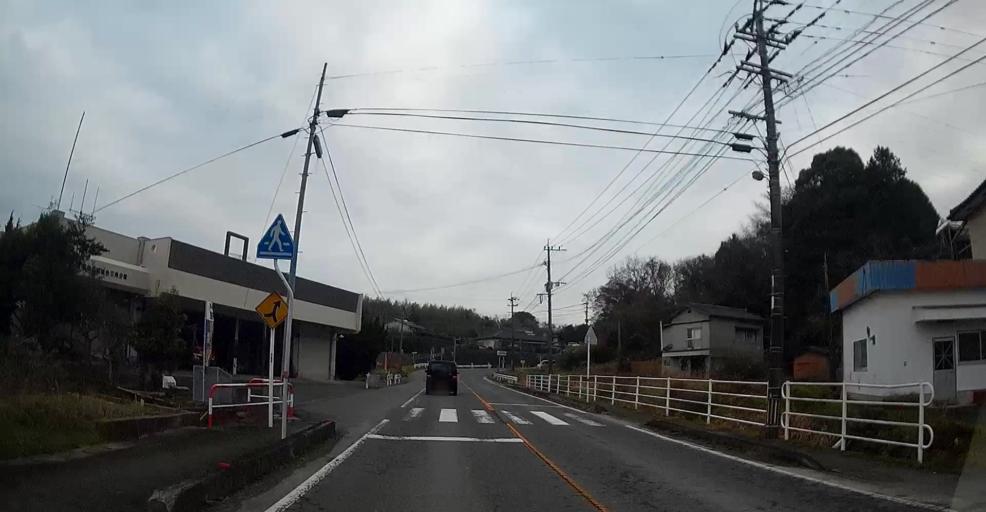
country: JP
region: Kumamoto
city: Yatsushiro
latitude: 32.6158
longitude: 130.5054
